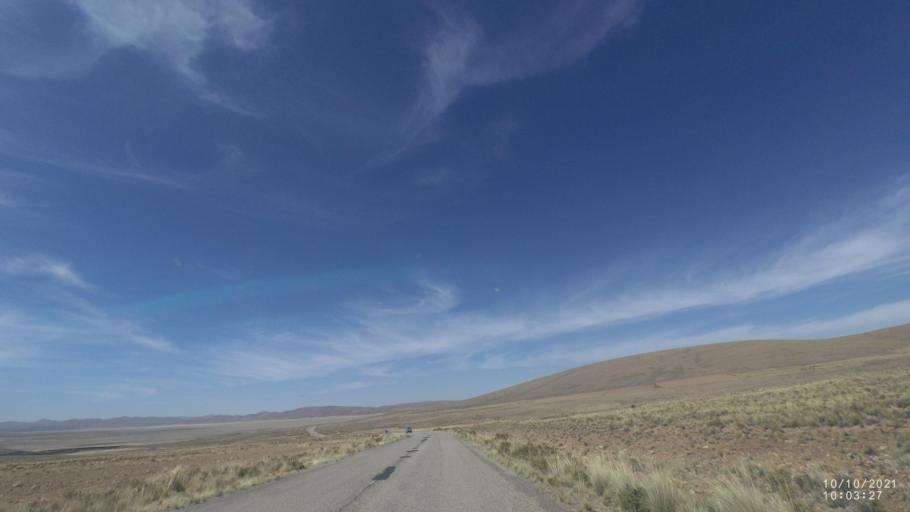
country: BO
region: La Paz
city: Eucaliptus
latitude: -17.3696
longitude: -67.4403
